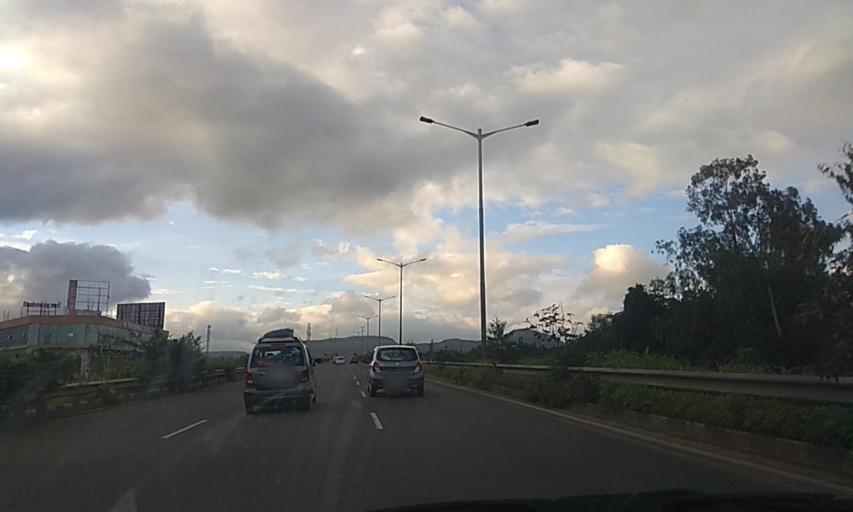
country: IN
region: Maharashtra
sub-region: Satara Division
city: Satara
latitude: 17.6243
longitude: 74.0174
